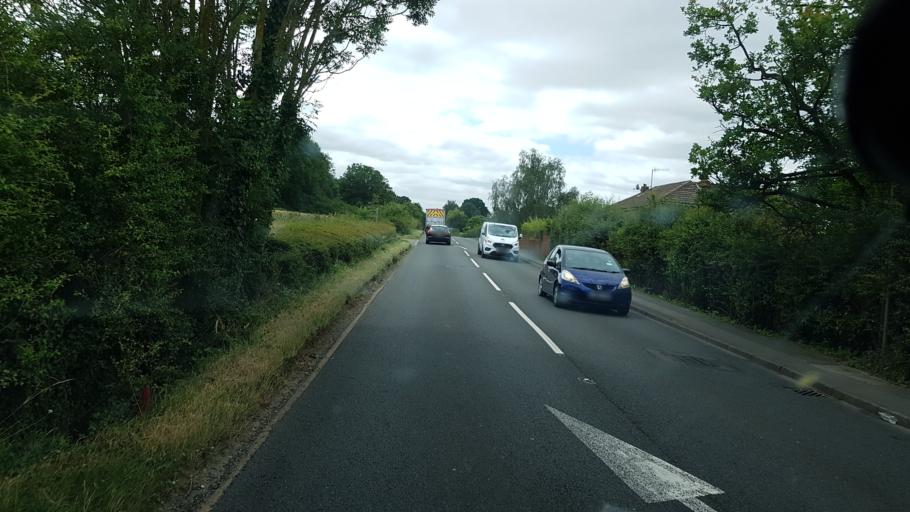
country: GB
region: England
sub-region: Surrey
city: Godstone
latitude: 51.2172
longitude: -0.0502
